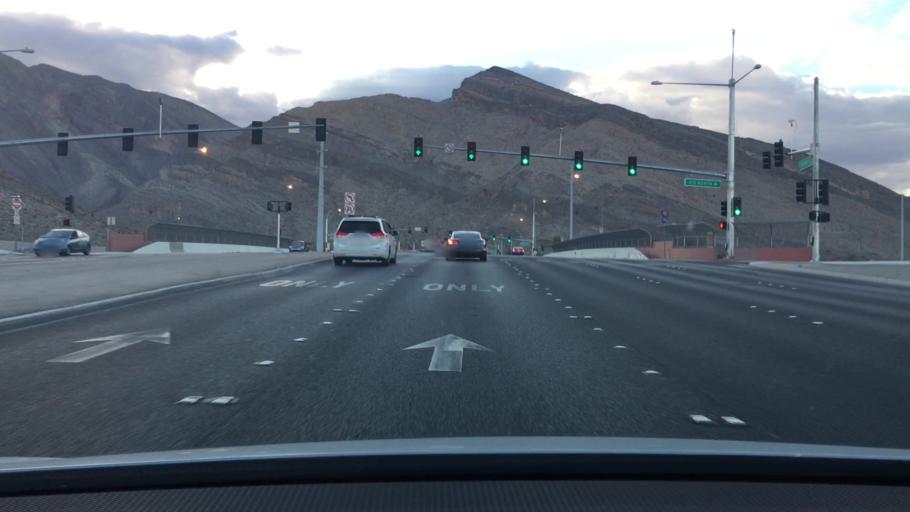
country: US
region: Nevada
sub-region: Clark County
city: Summerlin South
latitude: 36.2188
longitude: -115.3265
